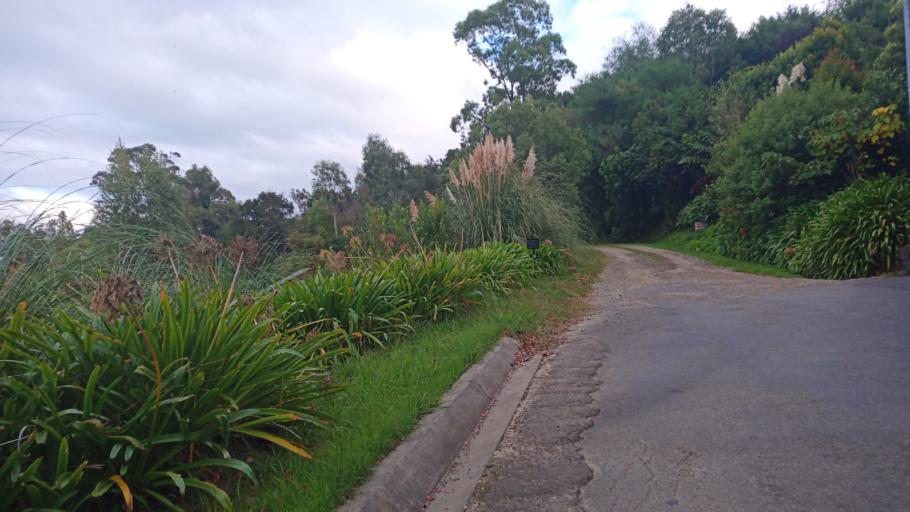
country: NZ
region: Gisborne
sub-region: Gisborne District
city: Gisborne
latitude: -38.6487
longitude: 178.0292
